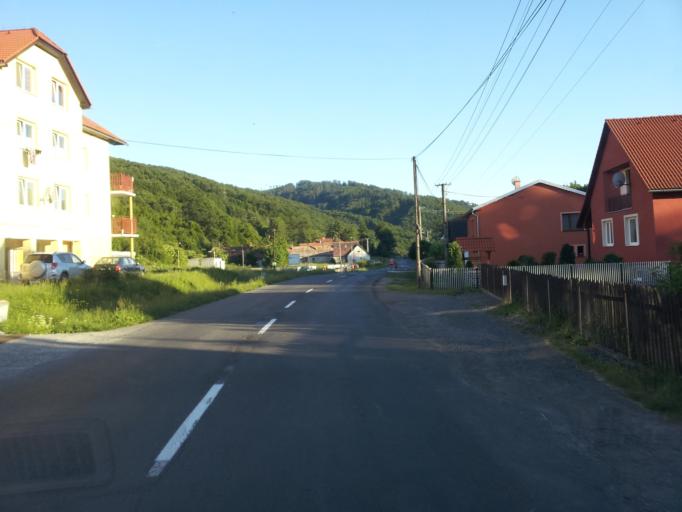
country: SK
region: Banskobystricky
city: Svaety Anton
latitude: 48.4073
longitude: 18.9405
